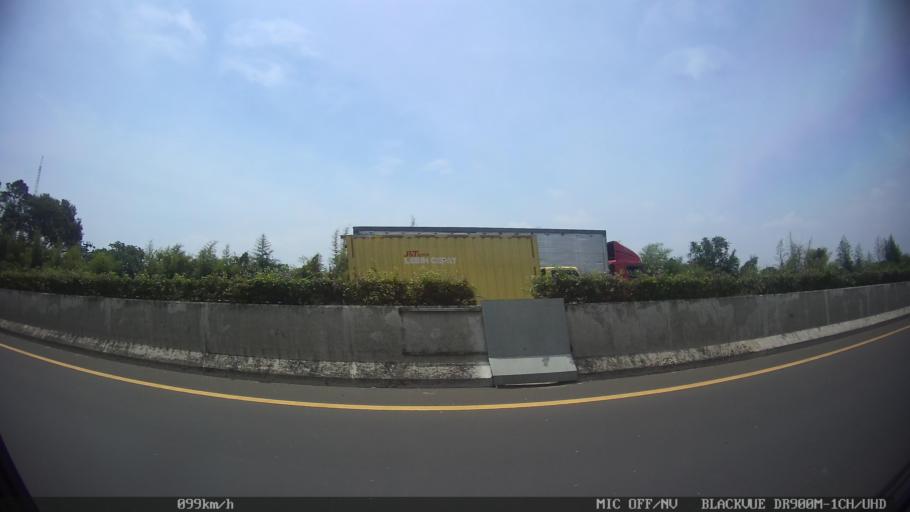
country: ID
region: West Java
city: Kresek
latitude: -6.1776
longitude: 106.3862
